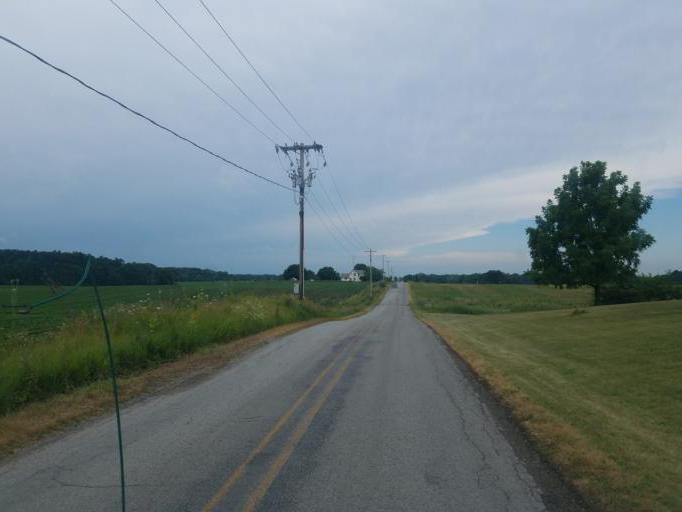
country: US
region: Indiana
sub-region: DeKalb County
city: Butler
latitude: 41.3707
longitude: -84.8885
